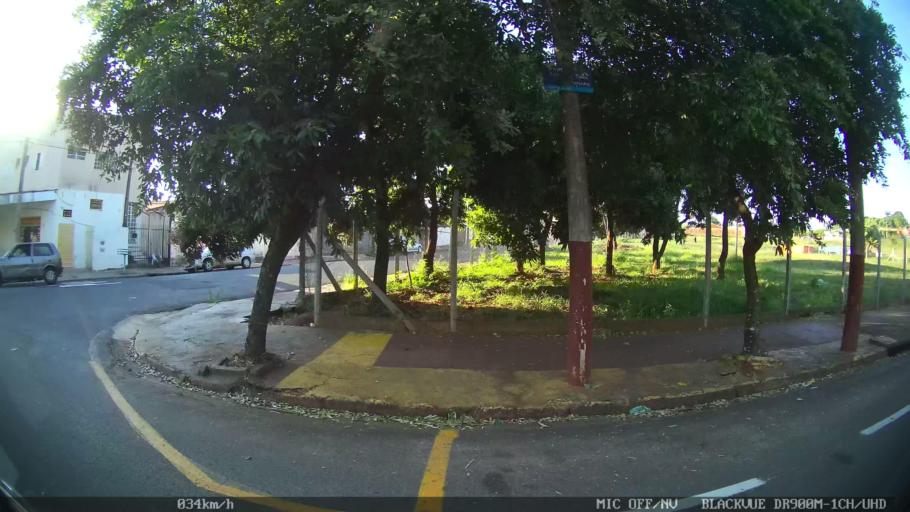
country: BR
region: Sao Paulo
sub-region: Sao Jose Do Rio Preto
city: Sao Jose do Rio Preto
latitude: -20.7870
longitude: -49.3656
